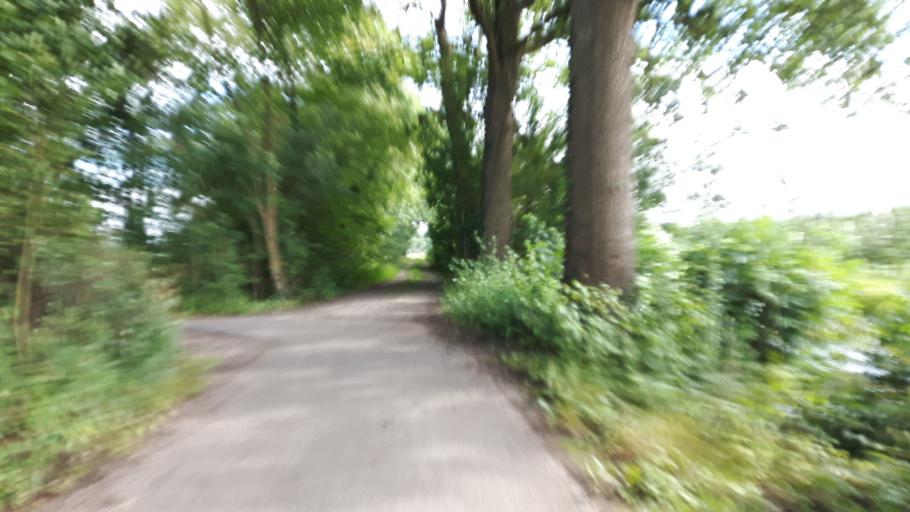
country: NL
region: Utrecht
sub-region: Gemeente Montfoort
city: Montfoort
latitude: 52.0938
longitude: 4.9708
